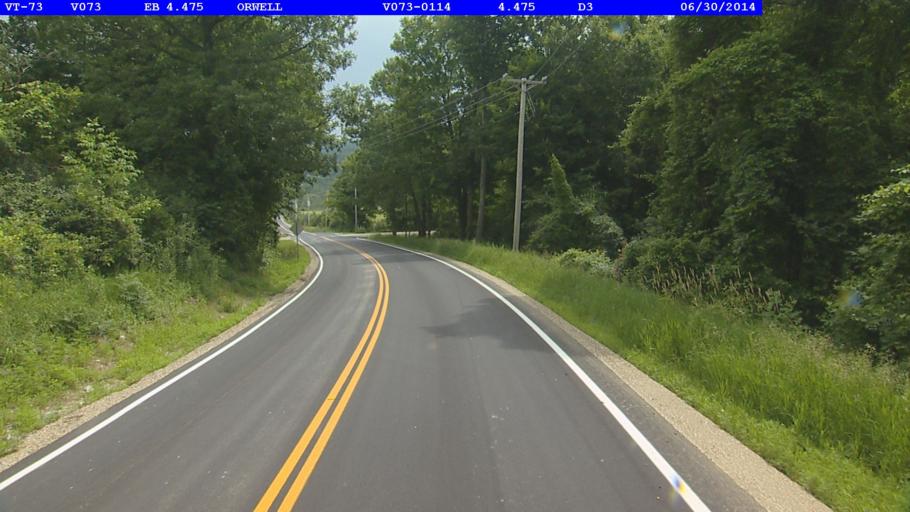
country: US
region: Vermont
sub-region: Rutland County
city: Brandon
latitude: 43.7944
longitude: -73.2214
